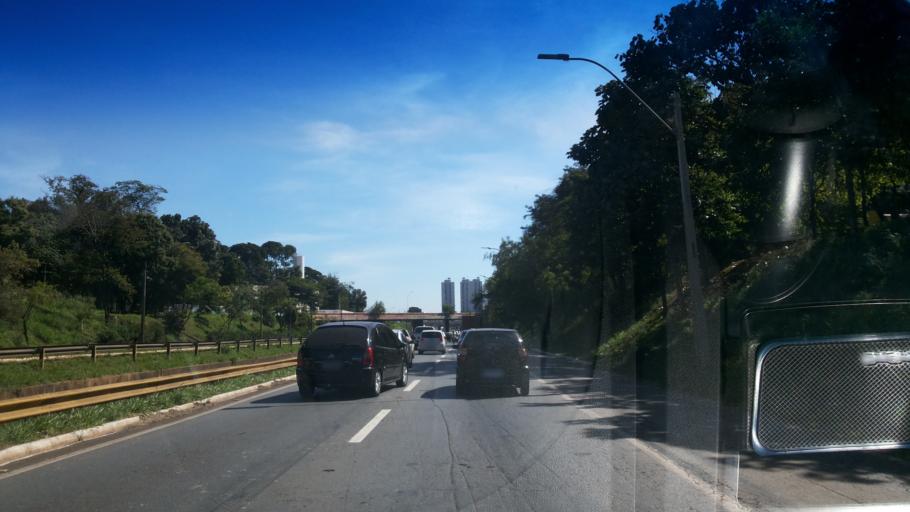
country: BR
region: Goias
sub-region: Goiania
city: Goiania
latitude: -16.6655
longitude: -49.2515
